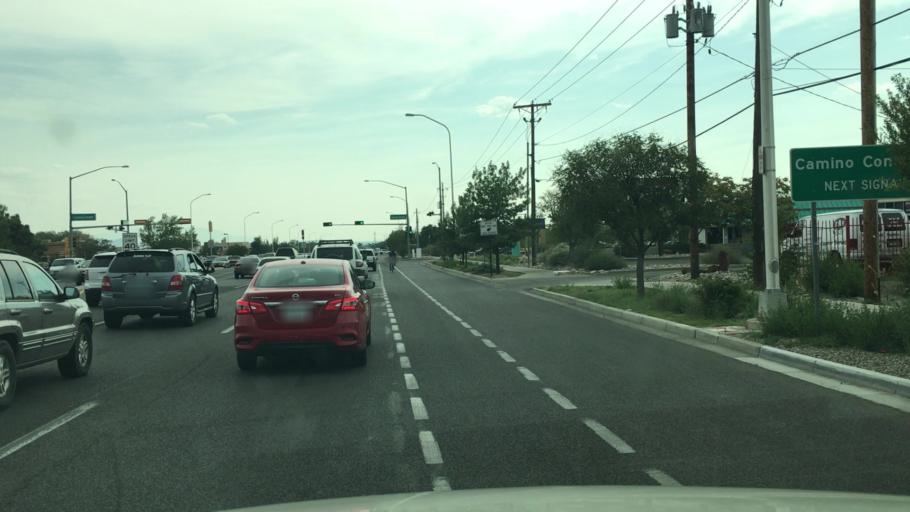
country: US
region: New Mexico
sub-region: Santa Fe County
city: Agua Fria
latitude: 35.6527
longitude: -105.9961
